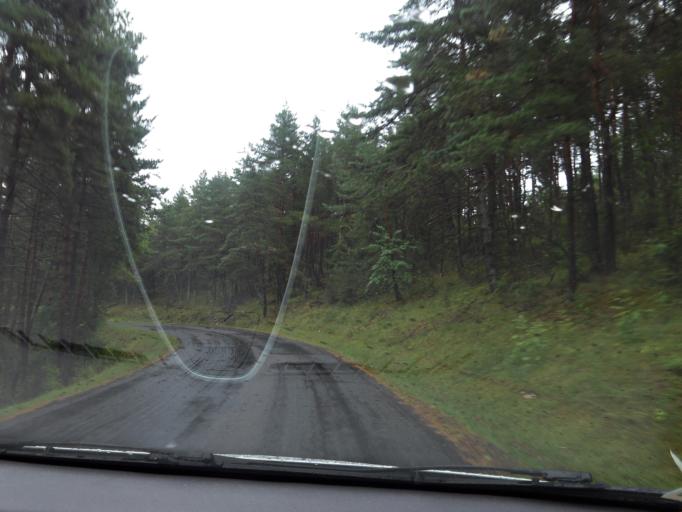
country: FR
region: Languedoc-Roussillon
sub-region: Departement de la Lozere
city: Mende
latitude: 44.4591
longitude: 3.4559
